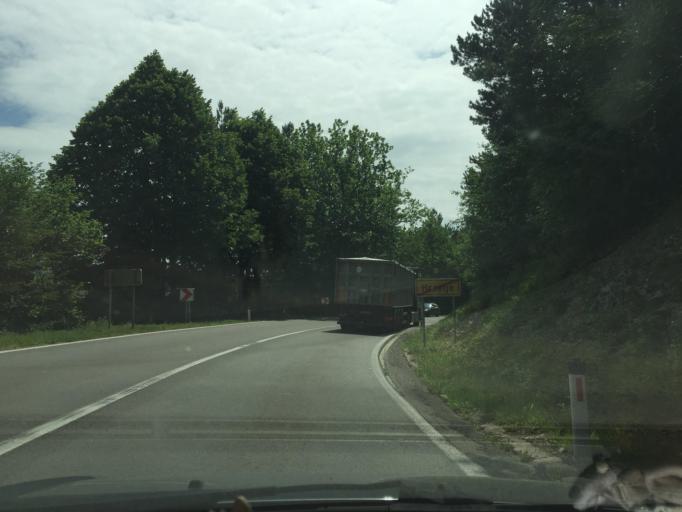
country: SI
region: Hrpelje-Kozina
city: Kozina
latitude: 45.6042
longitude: 13.9511
